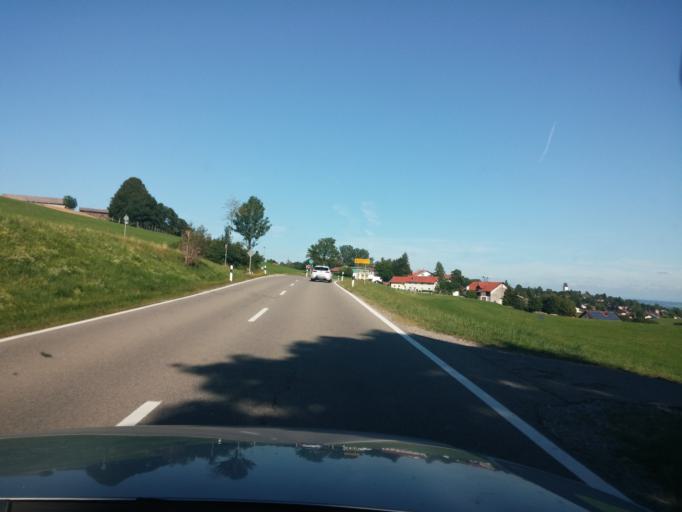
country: DE
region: Bavaria
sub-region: Swabia
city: Altusried
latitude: 47.8099
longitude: 10.1965
